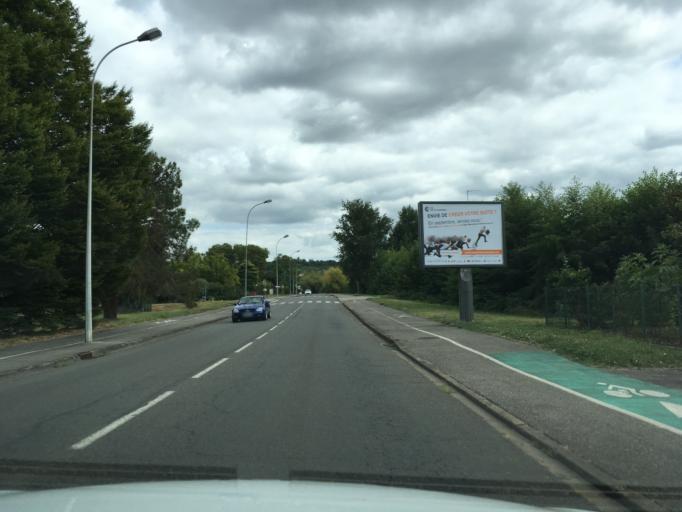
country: FR
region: Aquitaine
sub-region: Departement du Lot-et-Garonne
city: Agen
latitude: 44.2078
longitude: 0.6322
